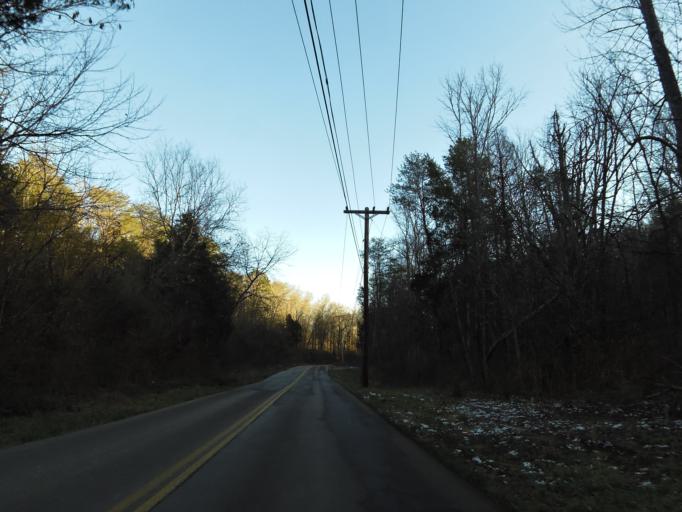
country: US
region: Tennessee
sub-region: Knox County
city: Farragut
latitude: 35.8840
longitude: -84.0970
